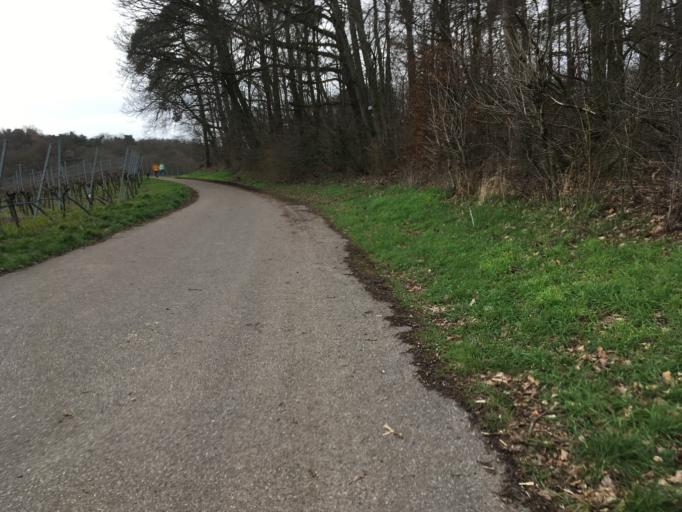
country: DE
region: Baden-Wuerttemberg
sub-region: Regierungsbezirk Stuttgart
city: Schwaigern
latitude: 49.1168
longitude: 9.0697
